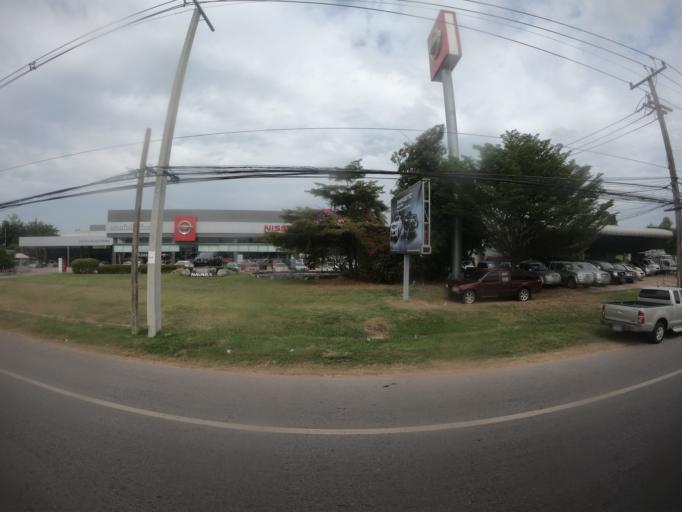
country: TH
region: Roi Et
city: Roi Et
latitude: 16.0619
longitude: 103.6233
